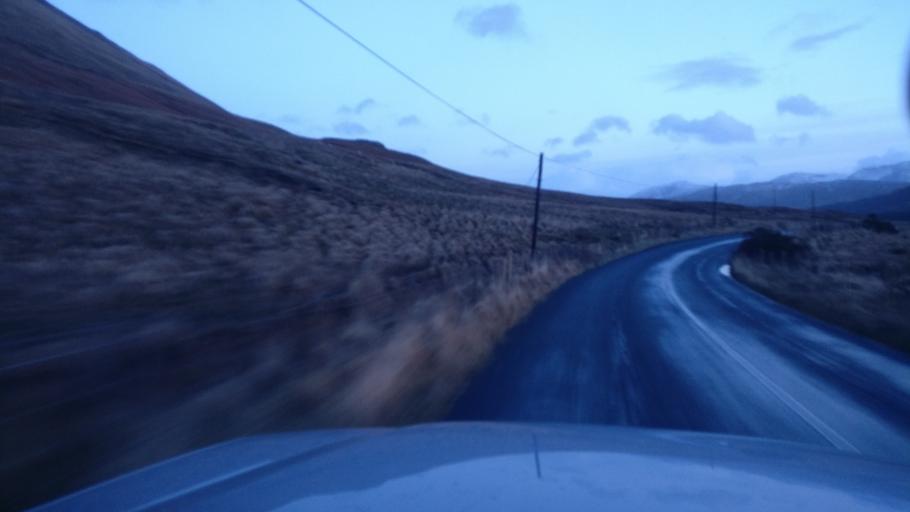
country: IE
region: Connaught
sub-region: Maigh Eo
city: Westport
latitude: 53.5636
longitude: -9.6496
